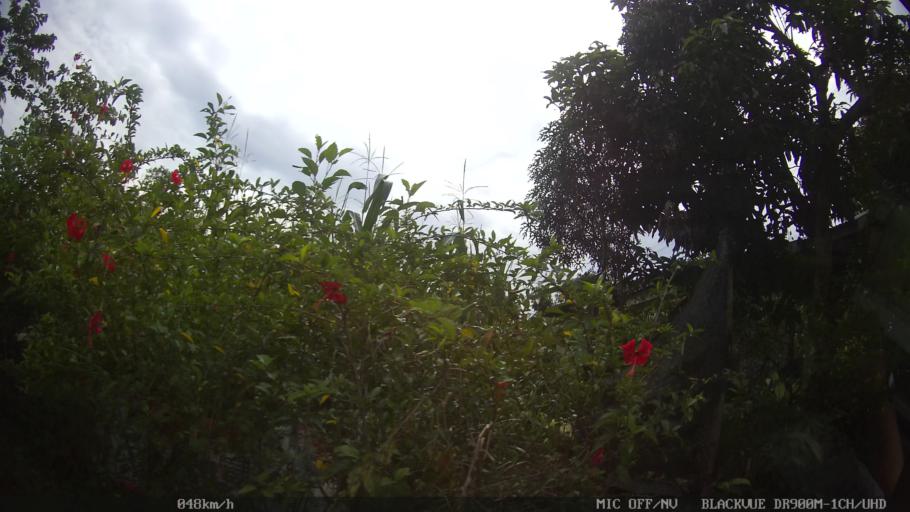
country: ID
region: North Sumatra
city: Sunggal
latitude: 3.5901
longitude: 98.5830
